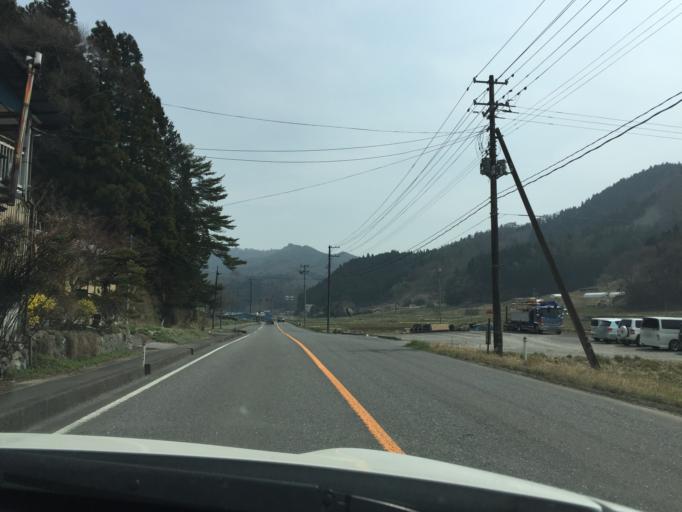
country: JP
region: Fukushima
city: Ishikawa
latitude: 37.0880
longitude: 140.5162
